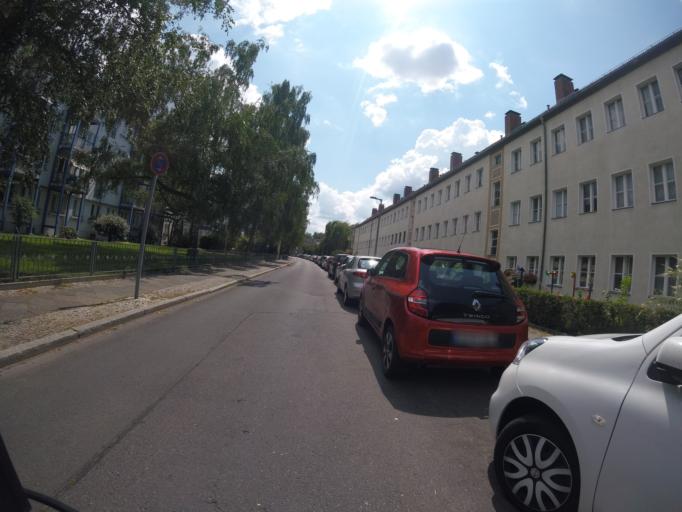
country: DE
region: Berlin
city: Charlottenburg-Nord
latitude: 52.5397
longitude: 13.2826
